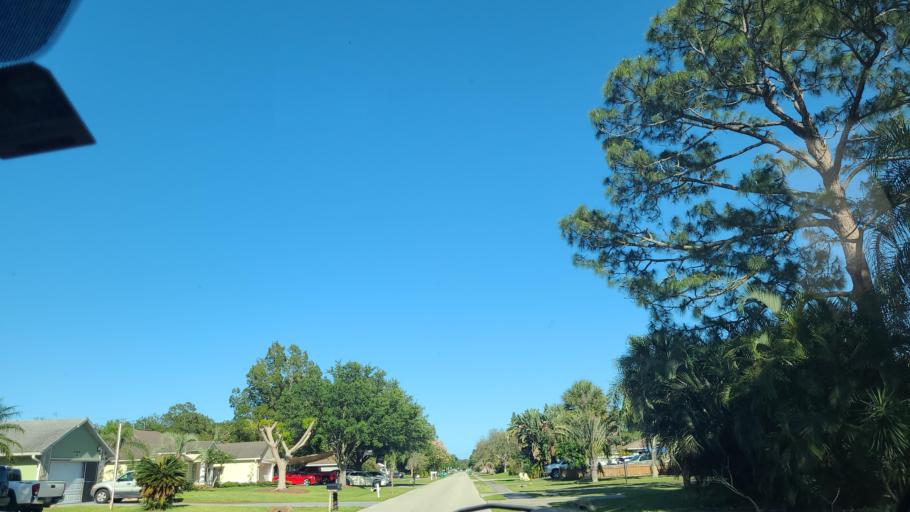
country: US
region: Florida
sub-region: Indian River County
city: Sebastian
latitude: 27.8000
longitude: -80.4905
